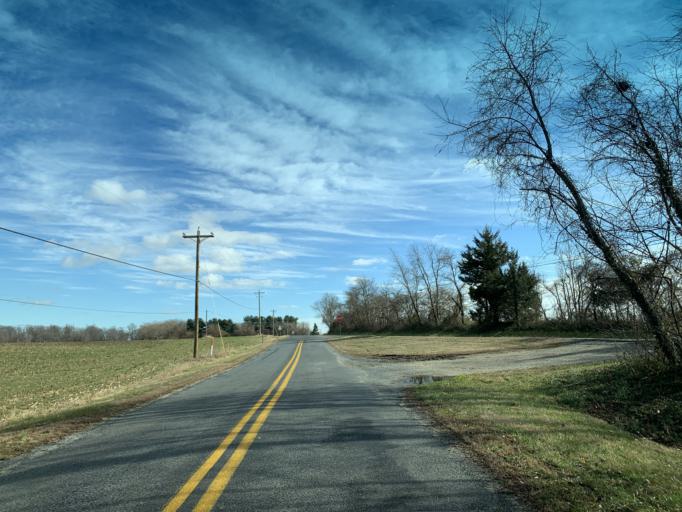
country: US
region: Maryland
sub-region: Kent County
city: Chestertown
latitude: 39.3278
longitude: -76.0395
